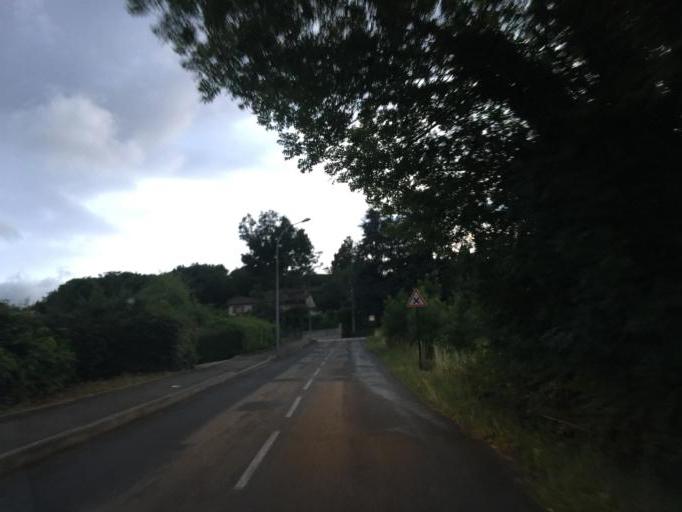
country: FR
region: Rhone-Alpes
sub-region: Departement de la Loire
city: Saint-Chamond
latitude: 45.4857
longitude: 4.5275
